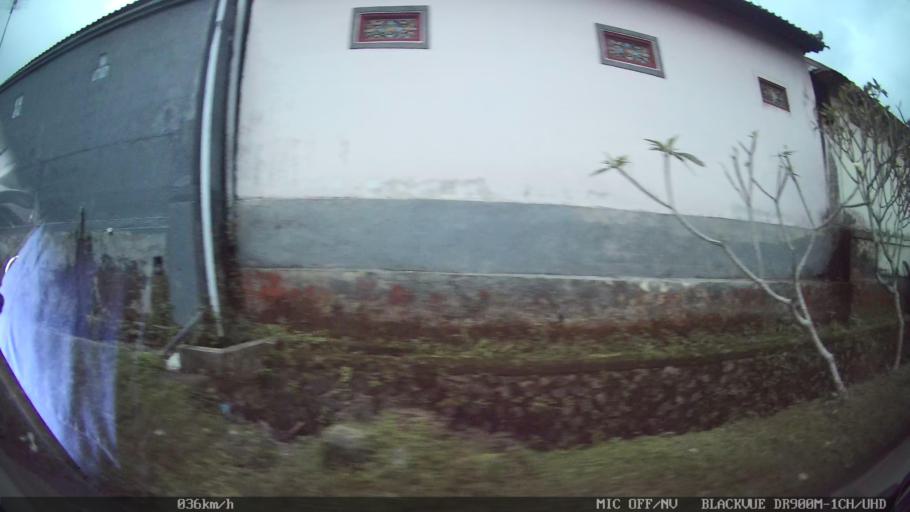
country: ID
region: Bali
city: Peneng
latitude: -8.3584
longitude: 115.2141
